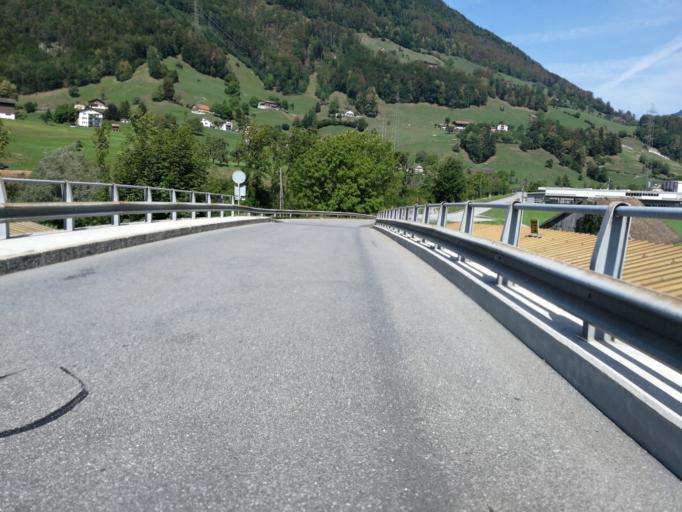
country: CH
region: Schwyz
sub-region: Bezirk Schwyz
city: Ingenbohl
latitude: 47.0073
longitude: 8.6183
